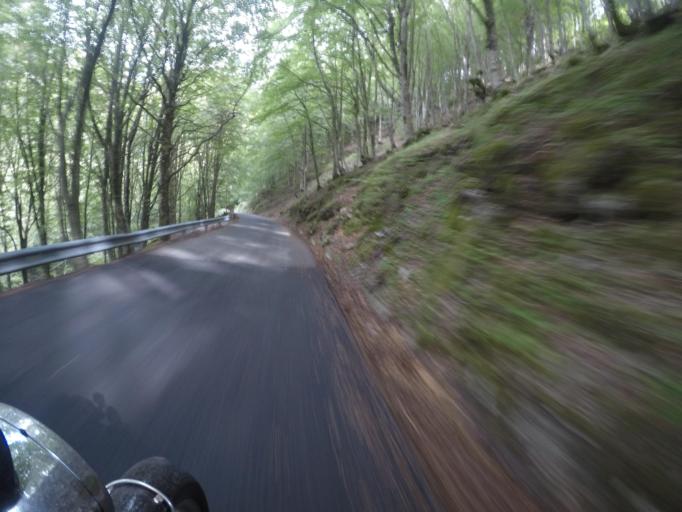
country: IT
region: Tuscany
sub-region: Provincia di Massa-Carrara
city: Carrara
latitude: 44.1154
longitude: 10.1186
